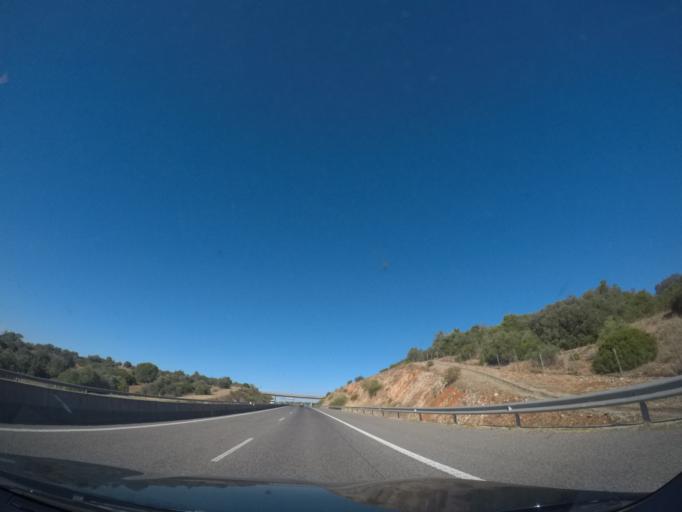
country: PT
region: Faro
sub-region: Portimao
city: Alvor
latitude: 37.1826
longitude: -8.5989
